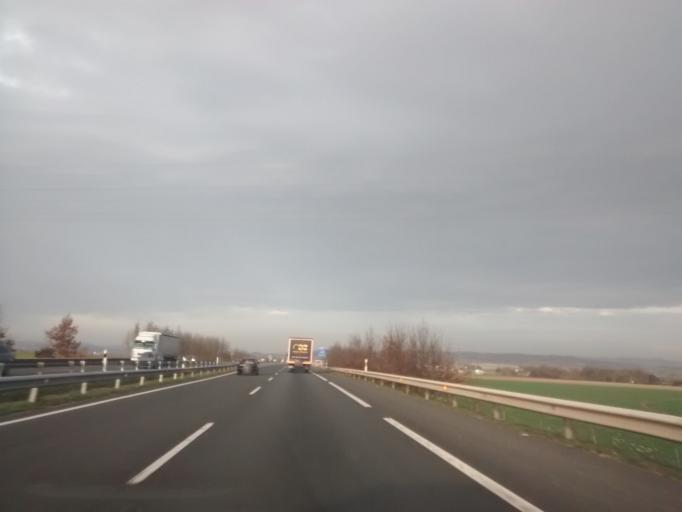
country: ES
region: Basque Country
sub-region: Provincia de Alava
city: Gasteiz / Vitoria
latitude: 42.8719
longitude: -2.7196
